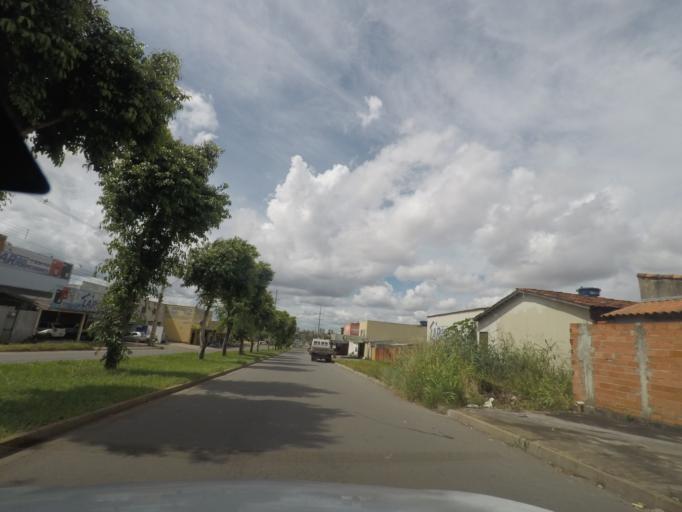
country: BR
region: Goias
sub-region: Goiania
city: Goiania
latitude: -16.7257
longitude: -49.3386
